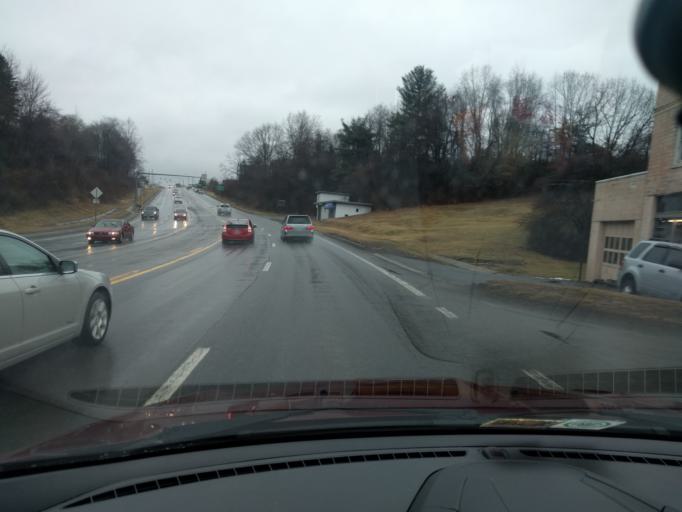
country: US
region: West Virginia
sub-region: Raleigh County
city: Beckley
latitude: 37.7898
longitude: -81.1848
